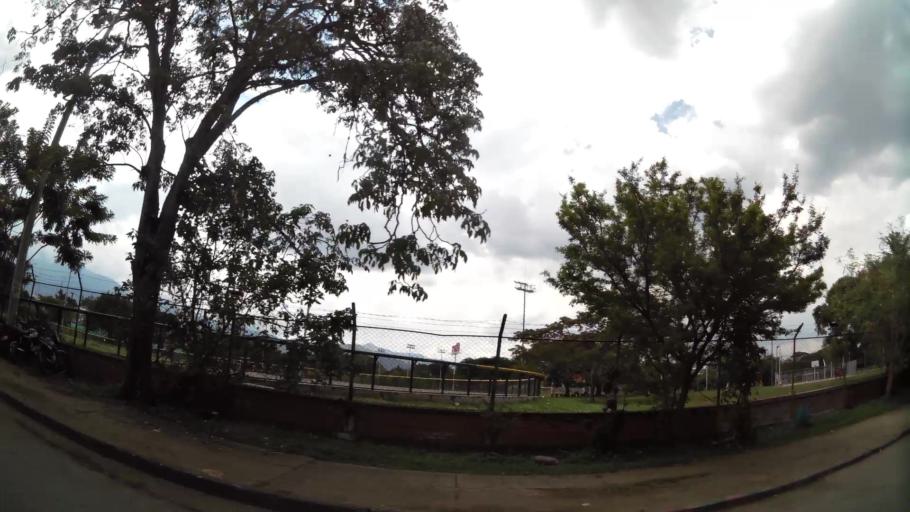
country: CO
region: Valle del Cauca
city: Cali
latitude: 3.4036
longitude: -76.5201
